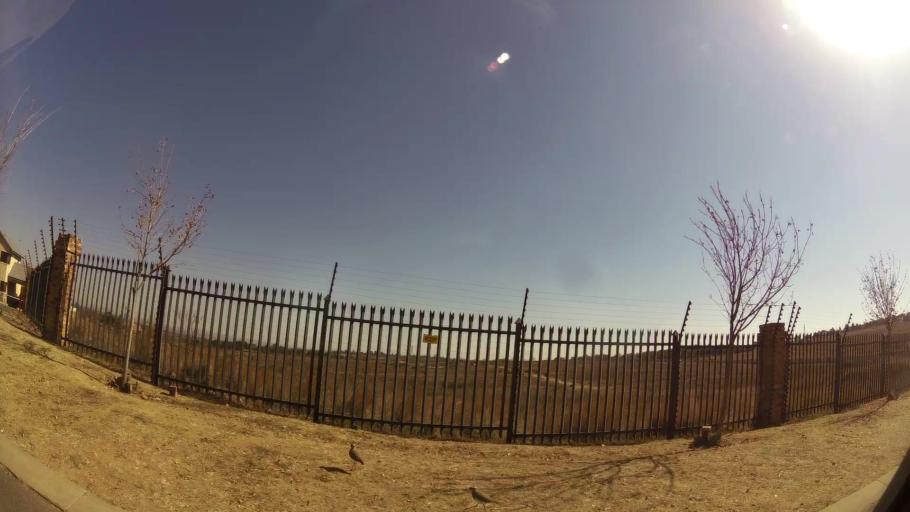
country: ZA
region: Gauteng
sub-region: City of Johannesburg Metropolitan Municipality
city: Midrand
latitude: -25.9501
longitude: 28.0826
